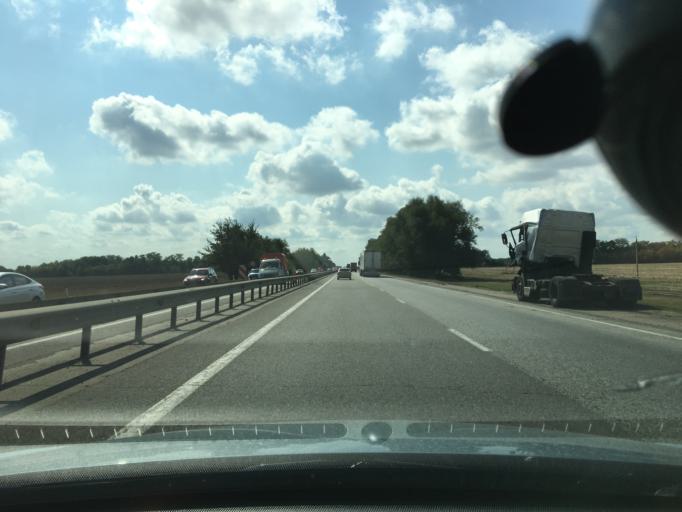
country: RU
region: Krasnodarskiy
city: Krasnoye
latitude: 46.6937
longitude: 39.6517
